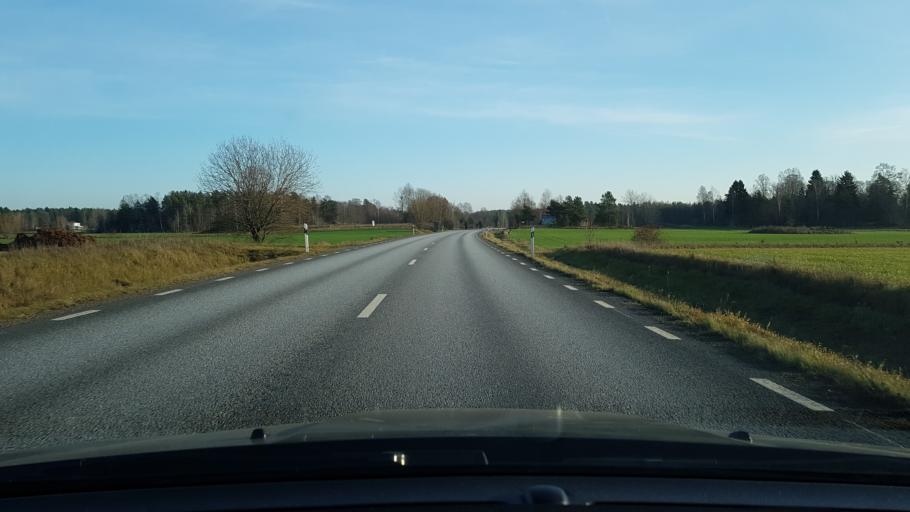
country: SE
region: Stockholm
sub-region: Vallentuna Kommun
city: Vallentuna
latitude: 59.7491
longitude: 18.0654
